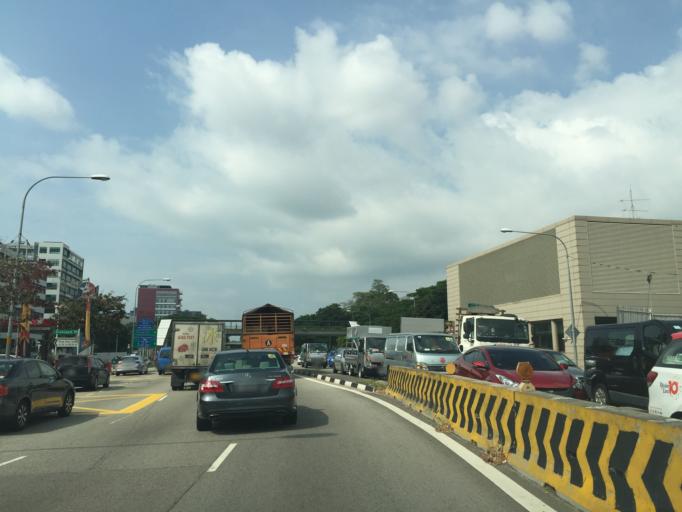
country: SG
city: Singapore
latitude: 1.3261
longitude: 103.8904
